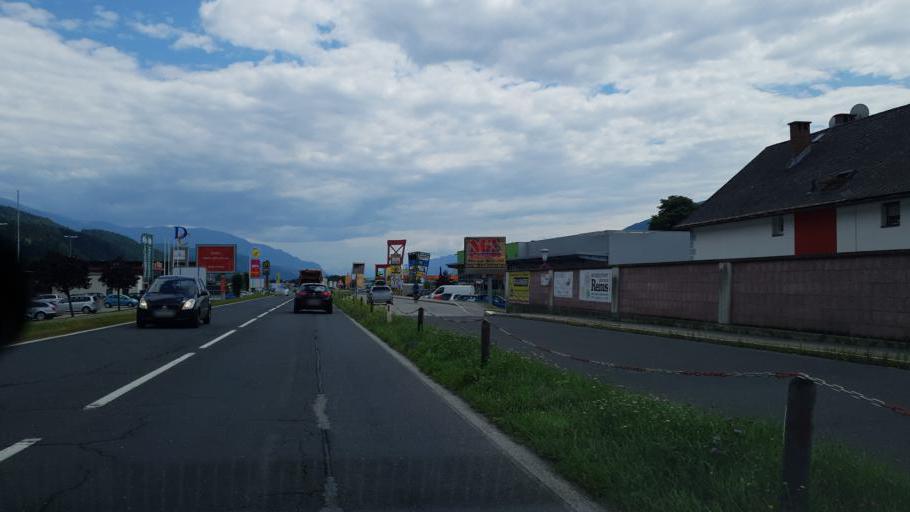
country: AT
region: Carinthia
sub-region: Politischer Bezirk Spittal an der Drau
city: Spittal an der Drau
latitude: 46.7877
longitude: 13.5204
